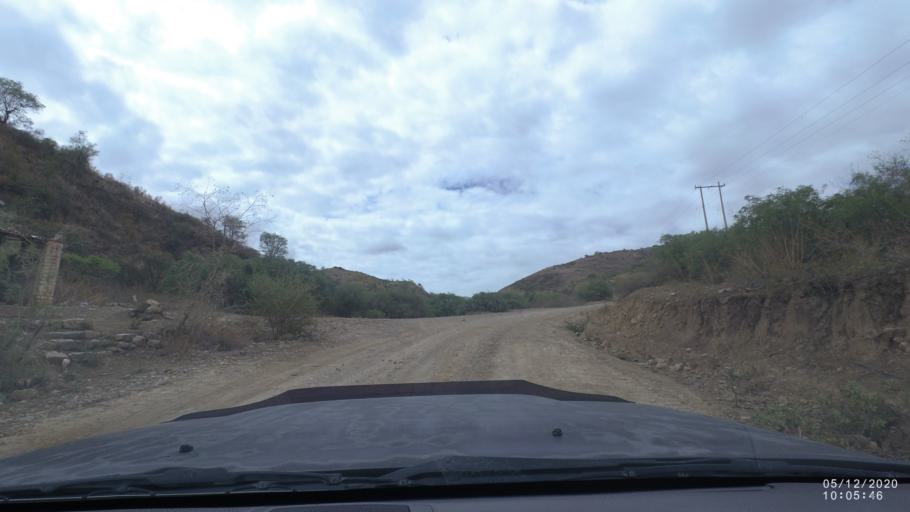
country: BO
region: Cochabamba
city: Sipe Sipe
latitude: -17.4720
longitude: -66.2844
